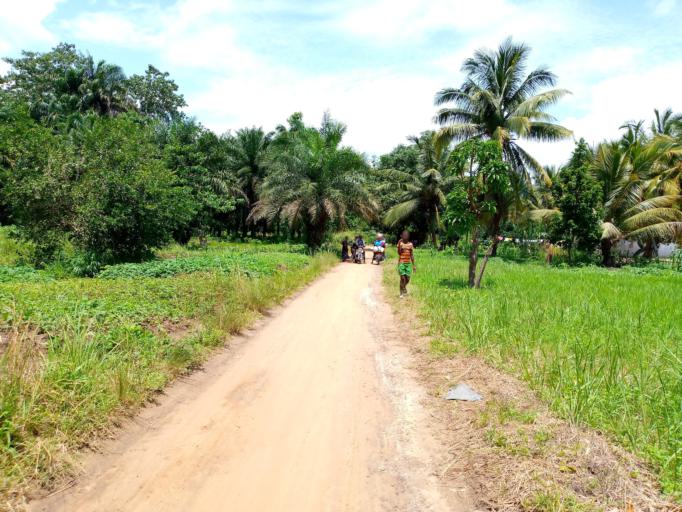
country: SL
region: Northern Province
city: Magburaka
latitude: 8.7090
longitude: -11.9594
